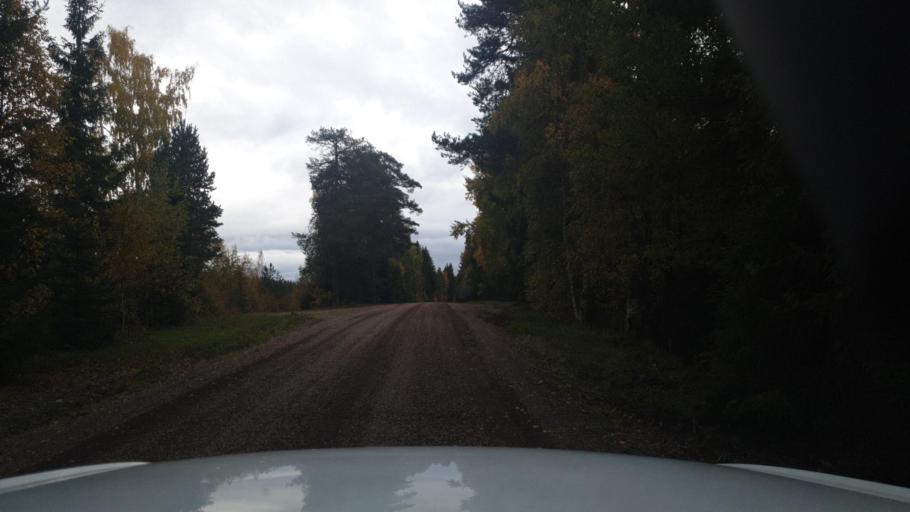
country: SE
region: Vaermland
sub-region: Eda Kommun
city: Charlottenberg
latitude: 60.0852
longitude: 12.5190
